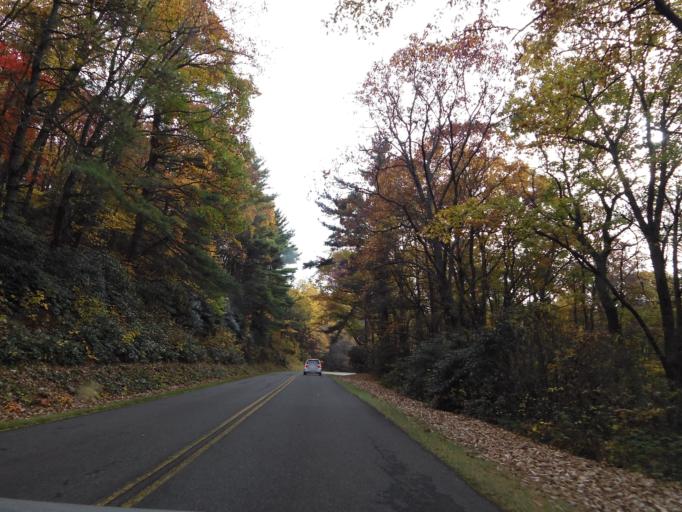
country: US
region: North Carolina
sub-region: Ashe County
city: Jefferson
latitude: 36.3060
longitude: -81.3627
